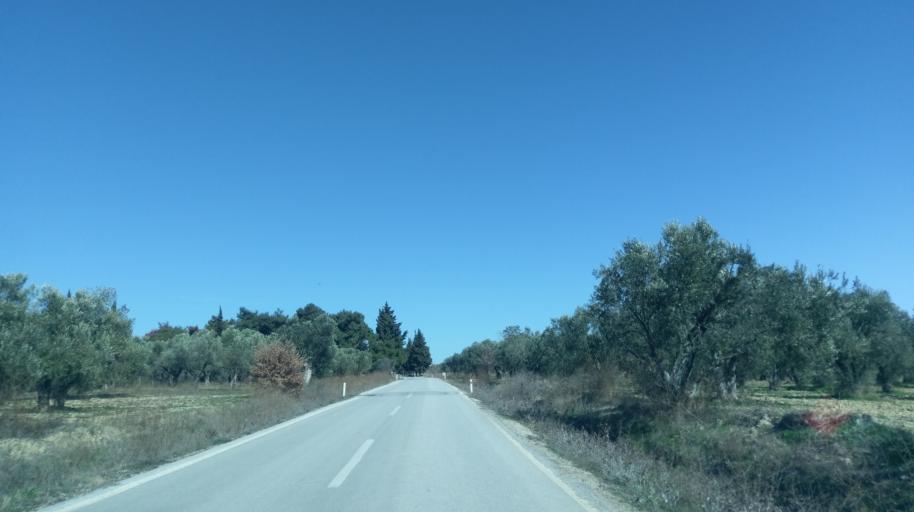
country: TR
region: Canakkale
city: Intepe
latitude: 40.0761
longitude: 26.2147
